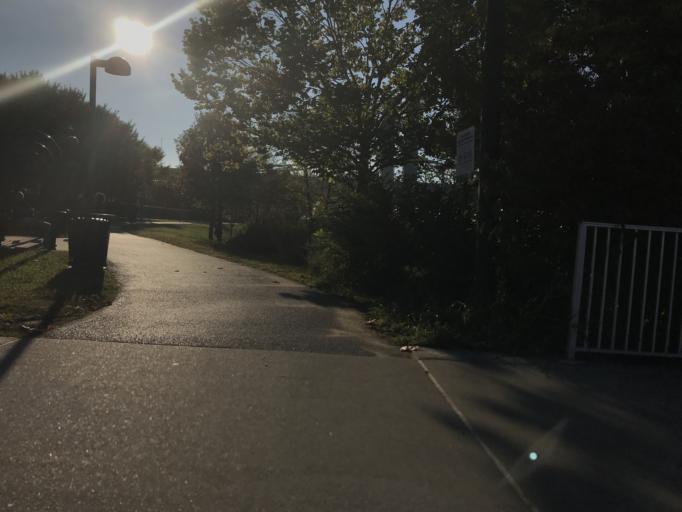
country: US
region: Indiana
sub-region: Clark County
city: Jeffersonville
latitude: 38.2626
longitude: -85.7385
